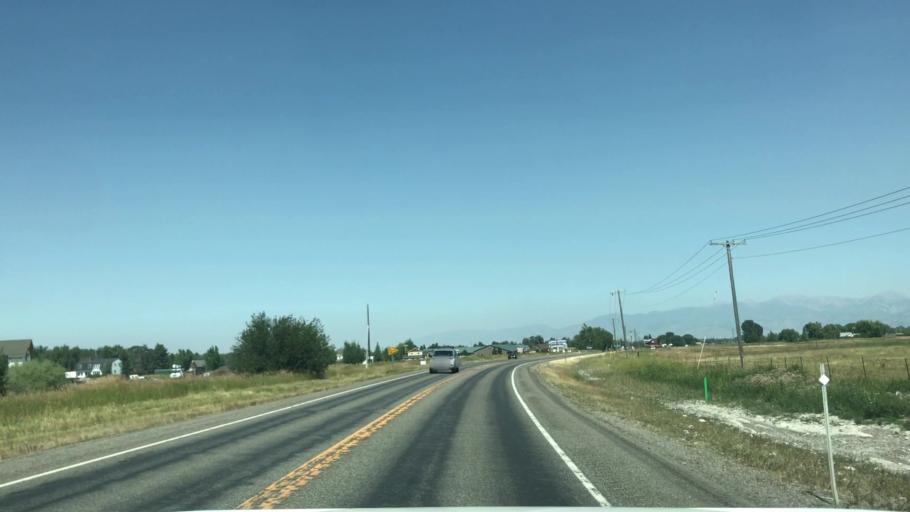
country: US
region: Montana
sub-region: Gallatin County
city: Four Corners
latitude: 45.6416
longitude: -111.1963
